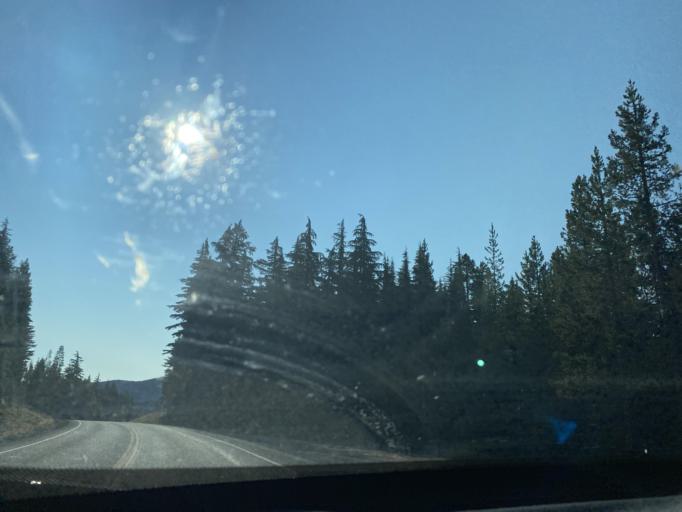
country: US
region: Oregon
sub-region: Deschutes County
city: Three Rivers
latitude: 43.7045
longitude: -121.2630
